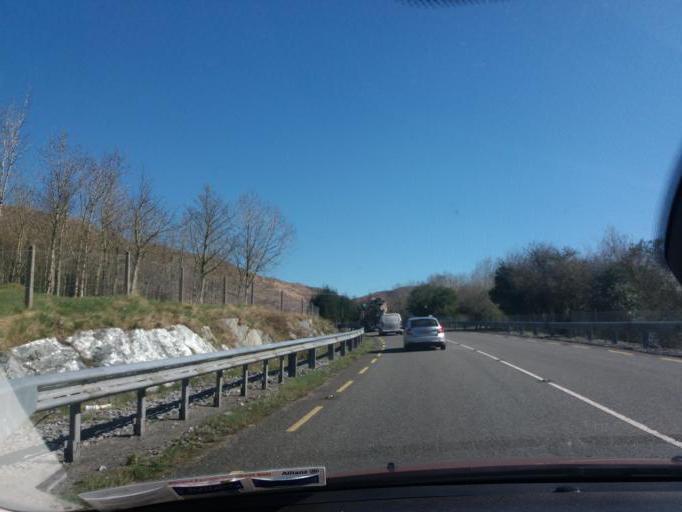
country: IE
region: Munster
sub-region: Ciarrai
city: Cill Airne
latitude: 51.9676
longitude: -9.3511
